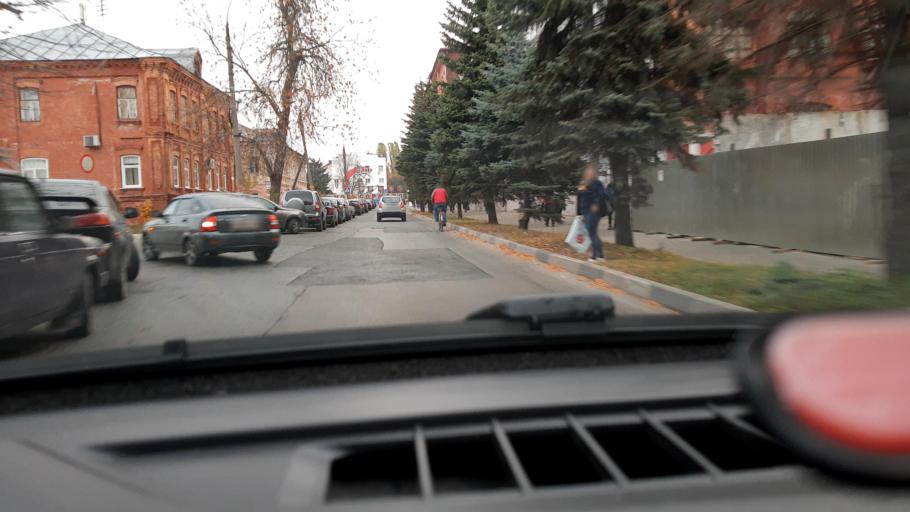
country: RU
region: Nizjnij Novgorod
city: Neklyudovo
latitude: 56.3580
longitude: 43.8689
